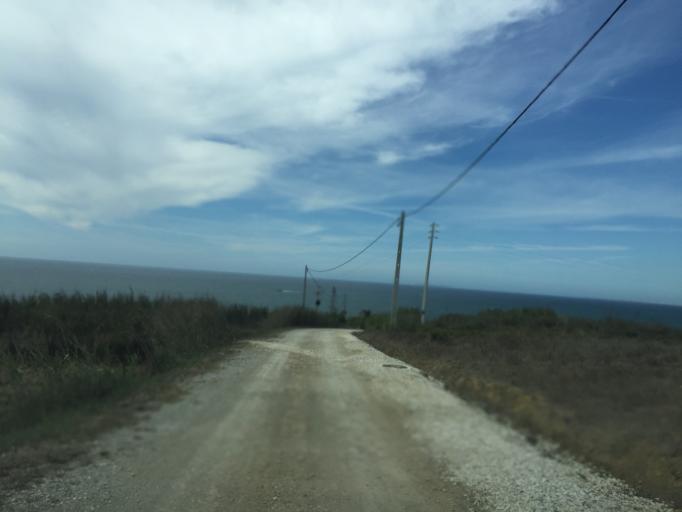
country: PT
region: Lisbon
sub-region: Lourinha
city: Lourinha
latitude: 39.1982
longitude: -9.3451
